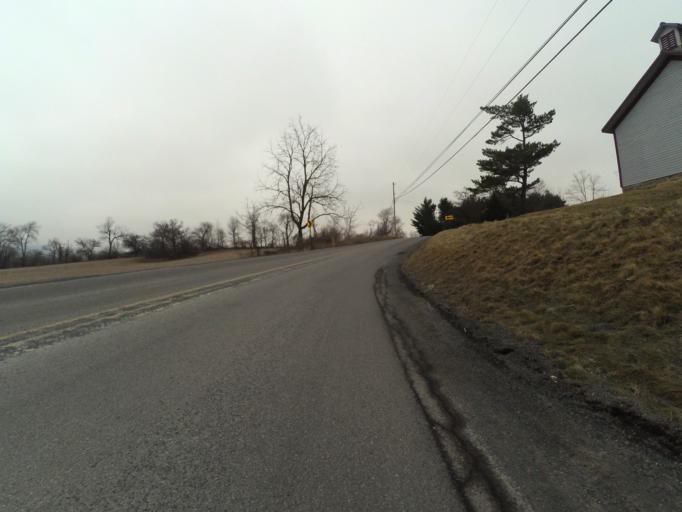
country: US
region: Pennsylvania
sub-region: Centre County
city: Boalsburg
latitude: 40.8000
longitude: -77.7623
